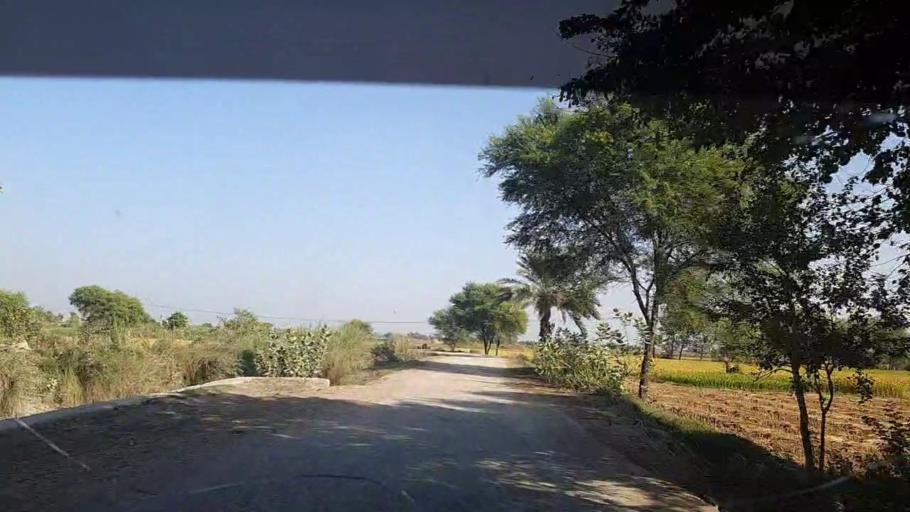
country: PK
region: Sindh
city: Larkana
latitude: 27.6217
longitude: 68.2449
